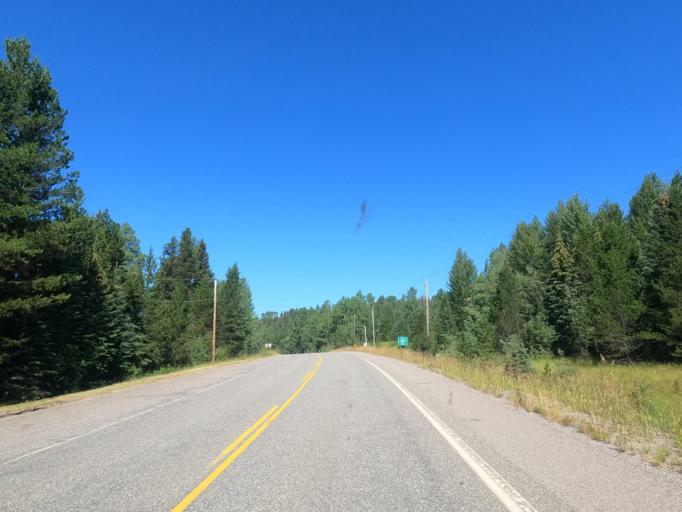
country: CA
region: British Columbia
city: Quesnel
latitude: 53.0514
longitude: -122.1542
